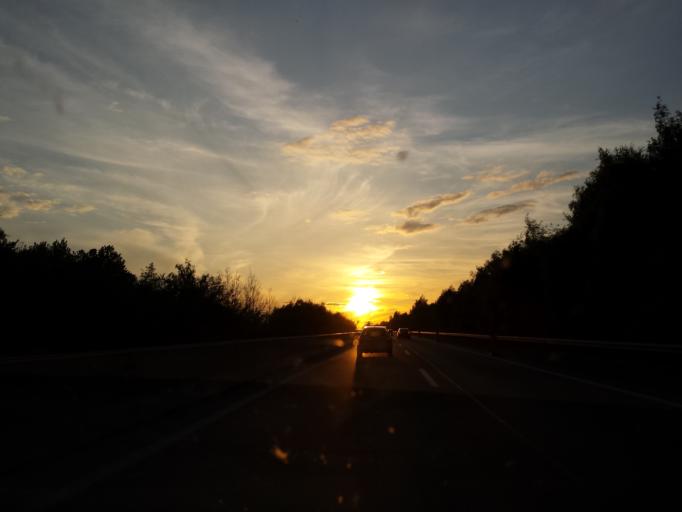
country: AT
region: Burgenland
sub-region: Politischer Bezirk Neusiedl am See
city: Bruckneudorf
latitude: 48.0393
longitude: 16.8004
